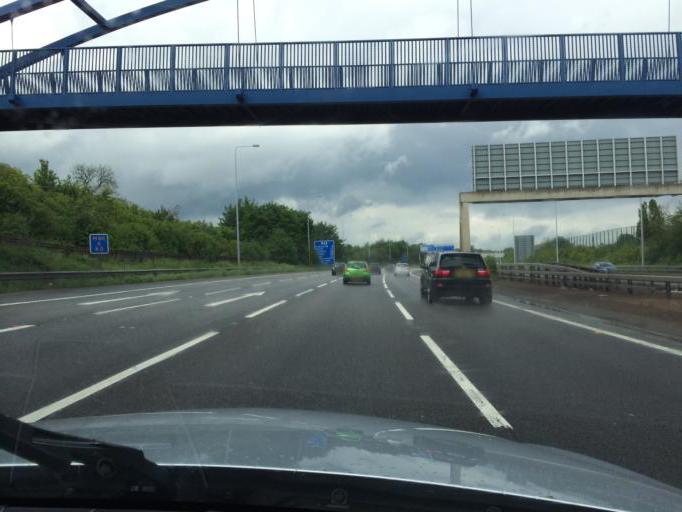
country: GB
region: England
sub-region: Manchester
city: Chorlton cum Hardy
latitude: 53.4149
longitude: -2.2793
